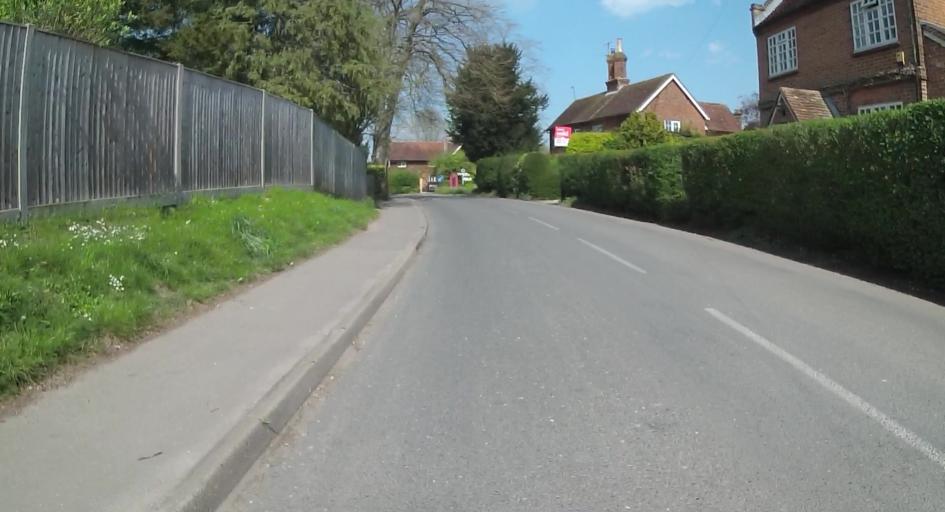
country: GB
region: England
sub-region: Hampshire
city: Basingstoke
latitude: 51.2945
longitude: -1.1062
